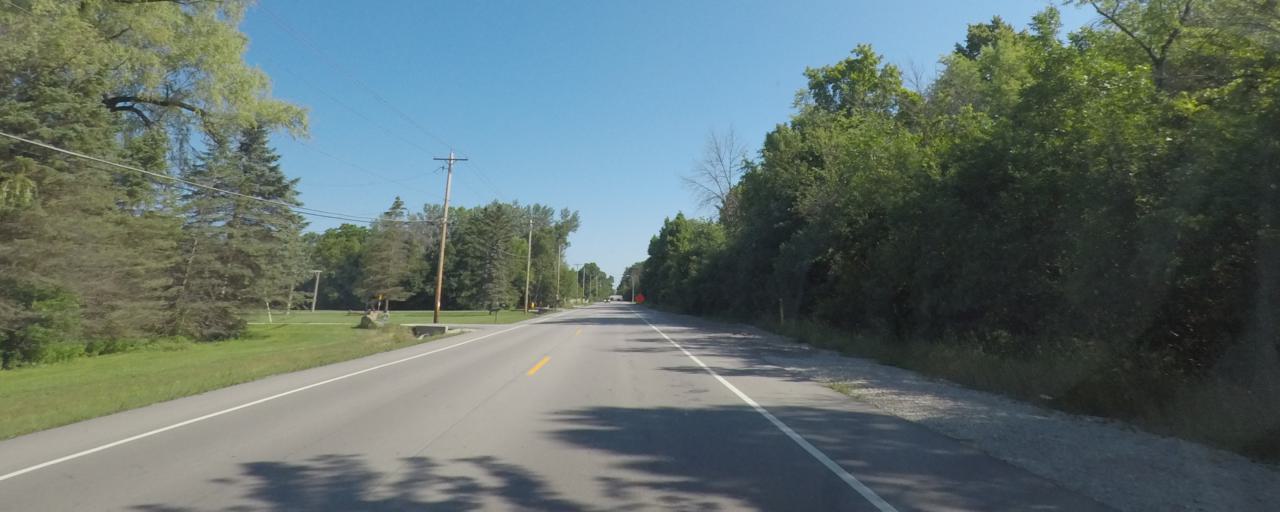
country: US
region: Wisconsin
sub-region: Waukesha County
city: Elm Grove
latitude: 43.0007
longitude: -88.0678
